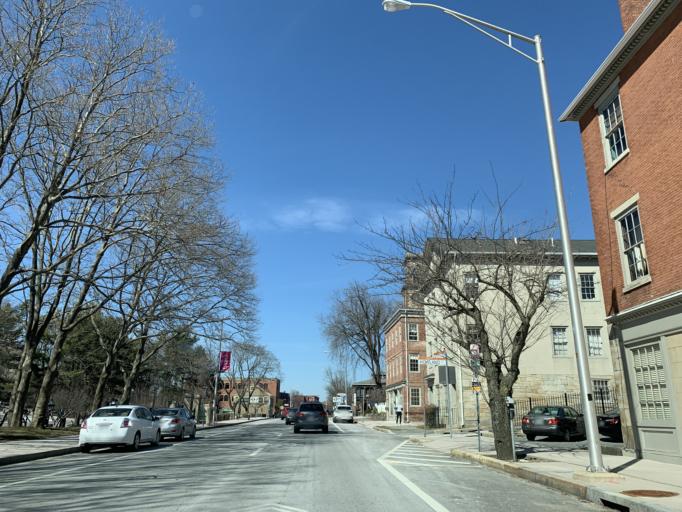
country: US
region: Rhode Island
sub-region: Providence County
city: Providence
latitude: 41.8301
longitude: -71.4101
